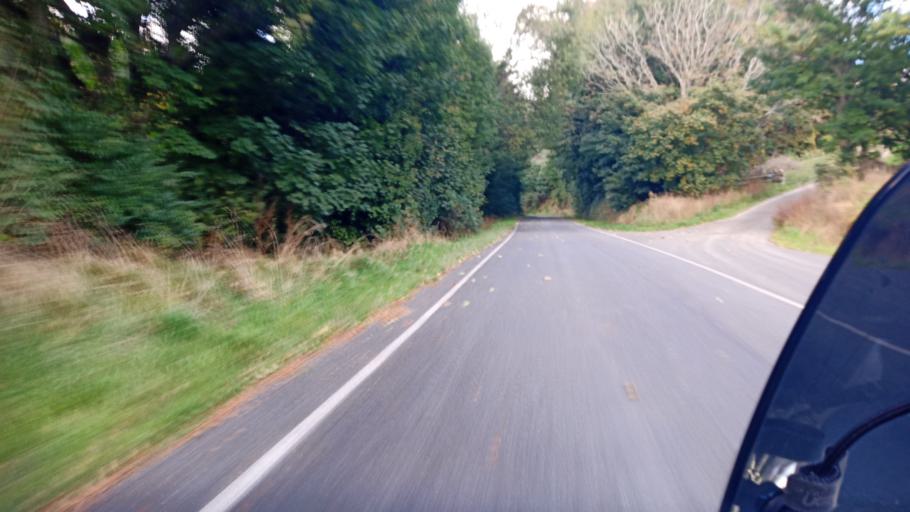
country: NZ
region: Gisborne
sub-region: Gisborne District
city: Gisborne
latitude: -38.5314
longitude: 177.5380
